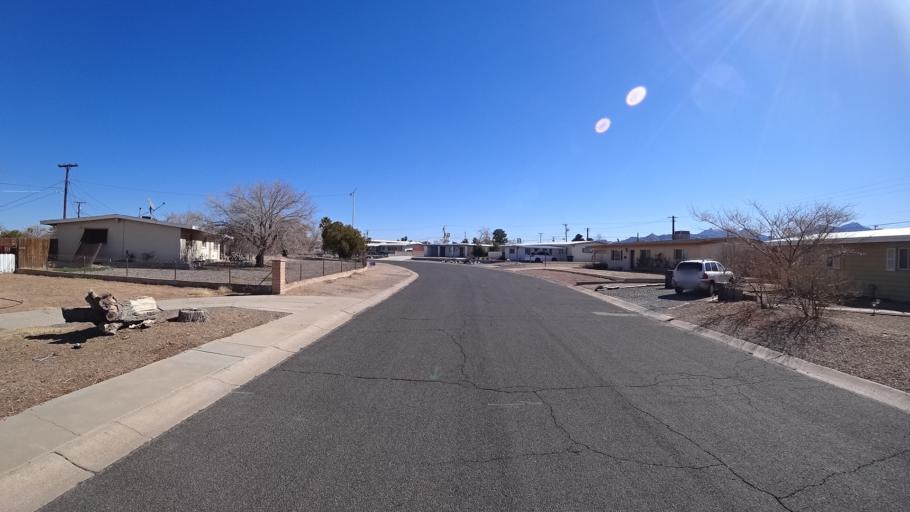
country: US
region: Arizona
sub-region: Mohave County
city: Kingman
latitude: 35.2109
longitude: -114.0200
